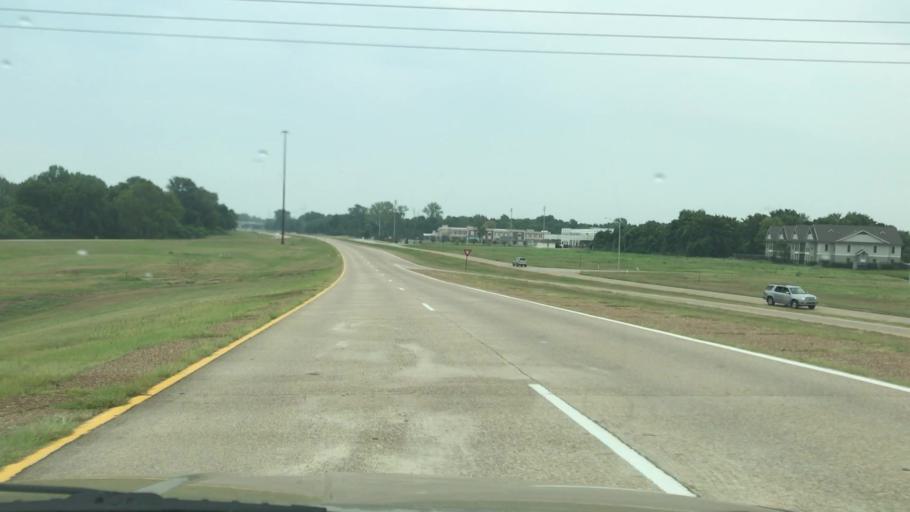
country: US
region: Louisiana
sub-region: Bossier Parish
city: Bossier City
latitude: 32.4996
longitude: -93.7149
